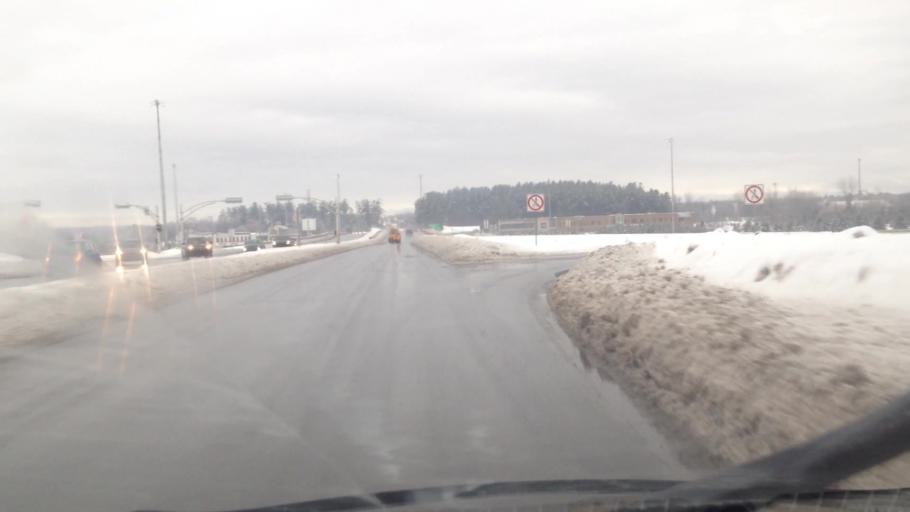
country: CA
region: Quebec
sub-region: Laurentides
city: Saint-Jerome
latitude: 45.7794
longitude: -74.0169
